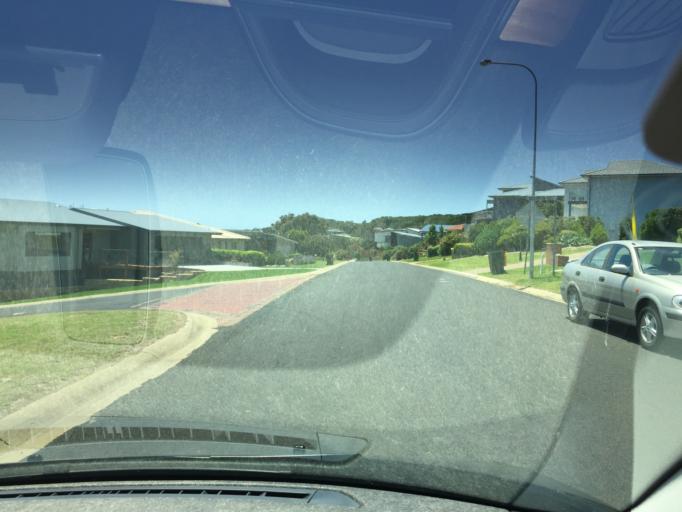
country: AU
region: New South Wales
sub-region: Bega Valley
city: Merimbula
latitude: -36.8506
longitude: 149.9319
